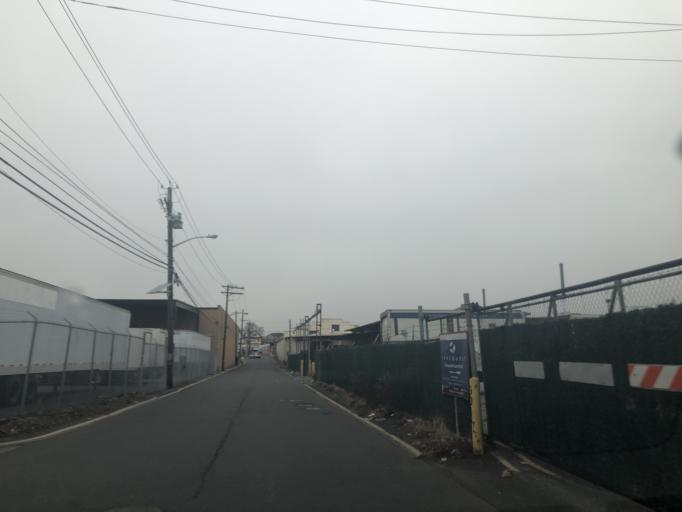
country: US
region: New Jersey
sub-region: Union County
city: Elizabeth
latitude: 40.6738
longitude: -74.1962
